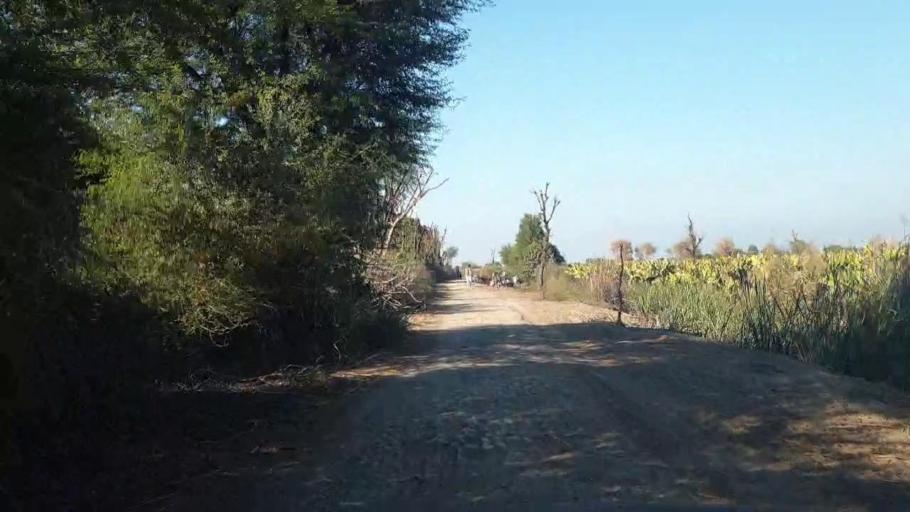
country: PK
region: Sindh
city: Shahdadpur
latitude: 25.9233
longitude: 68.5991
